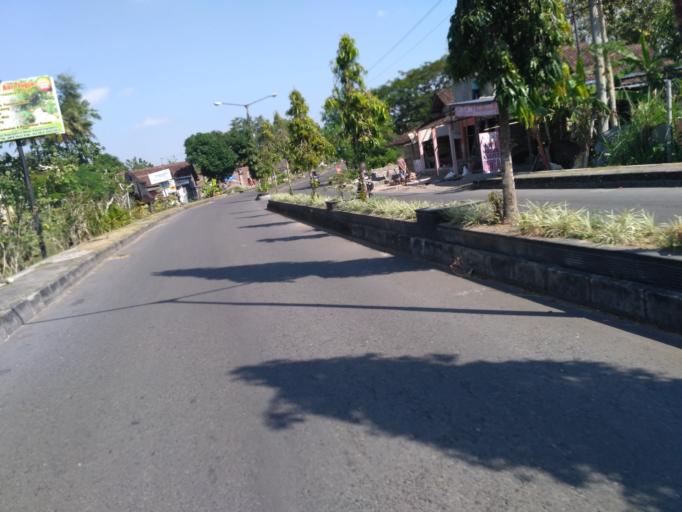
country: ID
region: Daerah Istimewa Yogyakarta
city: Depok
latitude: -7.7514
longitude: 110.4293
